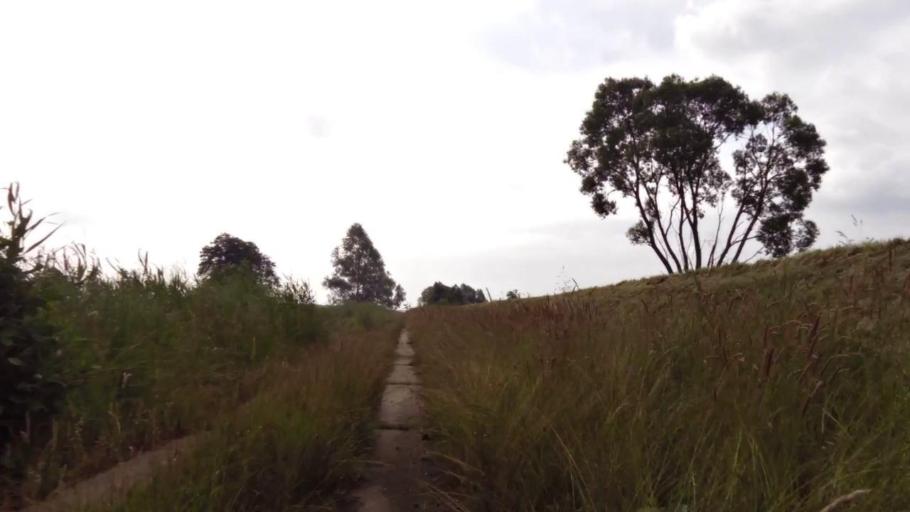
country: PL
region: West Pomeranian Voivodeship
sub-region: Powiat policki
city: Police
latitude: 53.5454
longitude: 14.6763
